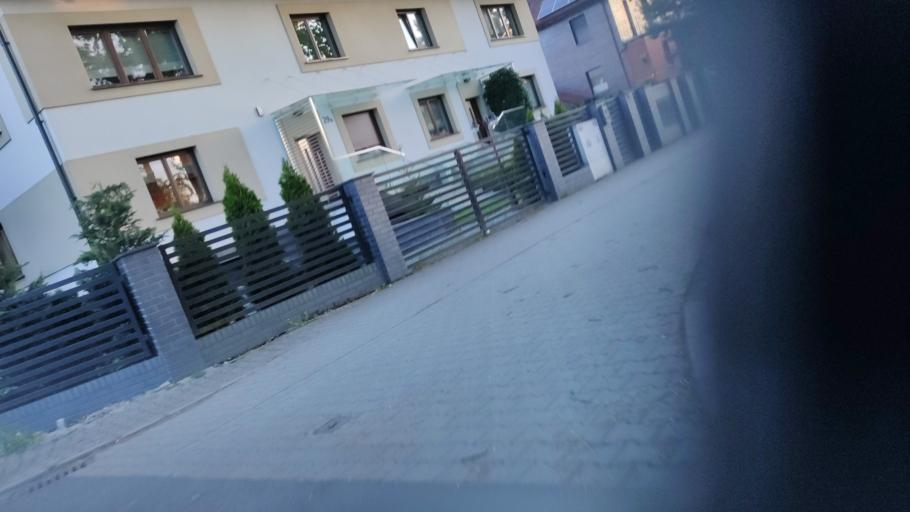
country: PL
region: Lower Silesian Voivodeship
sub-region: Powiat wroclawski
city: Wroclaw
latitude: 51.0744
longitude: 17.0384
